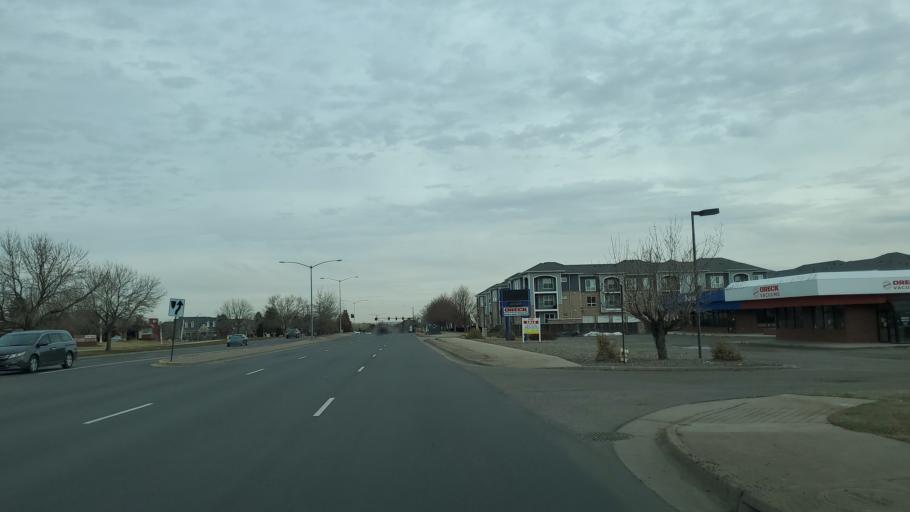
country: US
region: Colorado
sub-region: Adams County
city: Northglenn
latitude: 39.9138
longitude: -104.9562
